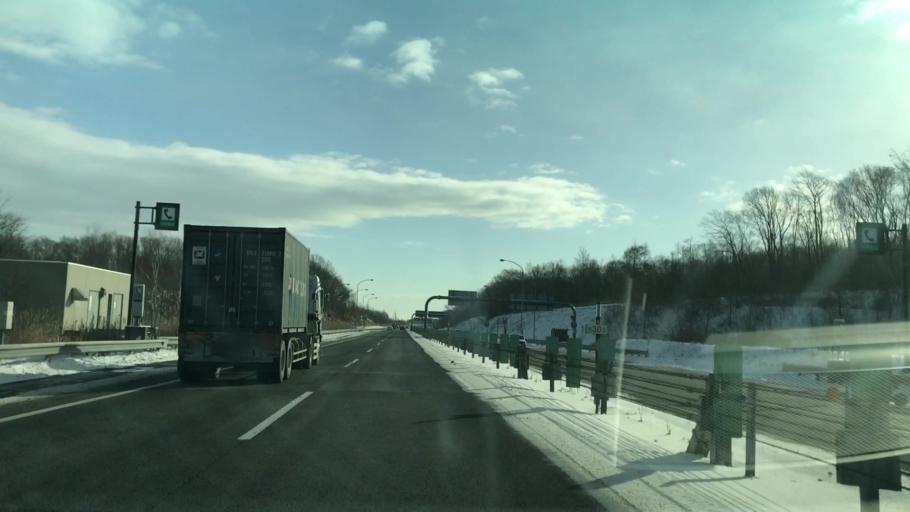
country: JP
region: Hokkaido
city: Chitose
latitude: 42.8447
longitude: 141.5870
